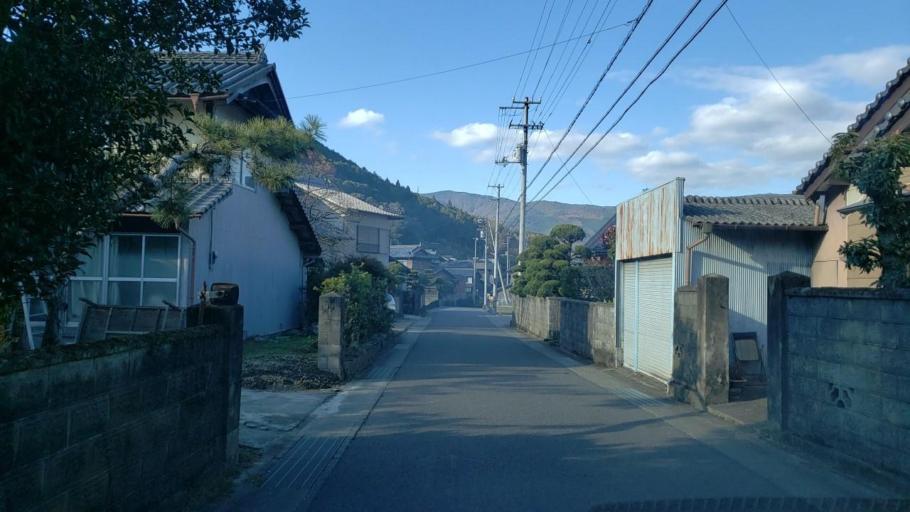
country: JP
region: Tokushima
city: Wakimachi
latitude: 34.0285
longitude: 134.0301
